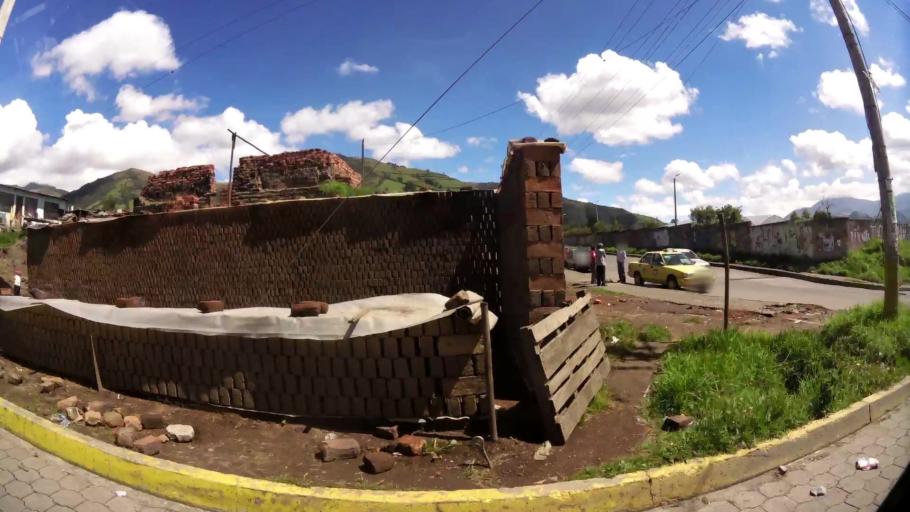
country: EC
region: Pichincha
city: Quito
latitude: -0.3219
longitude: -78.5648
